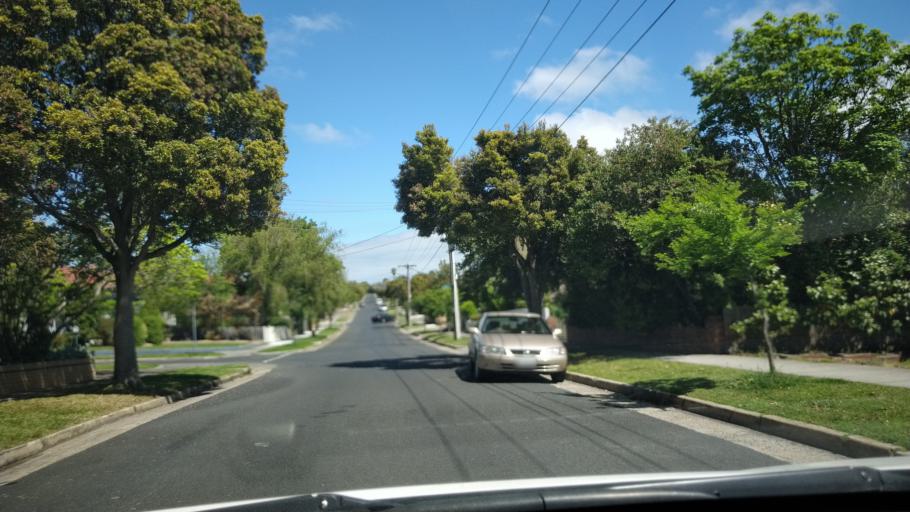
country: AU
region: Victoria
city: Murrumbeena
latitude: -37.9022
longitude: 145.0734
